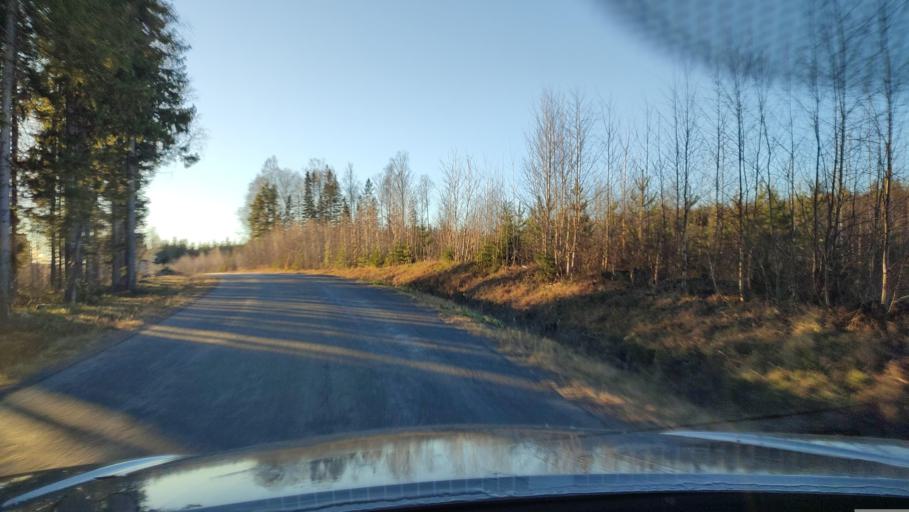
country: SE
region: Vaesterbotten
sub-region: Skelleftea Kommun
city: Viken
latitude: 64.7104
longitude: 20.9058
